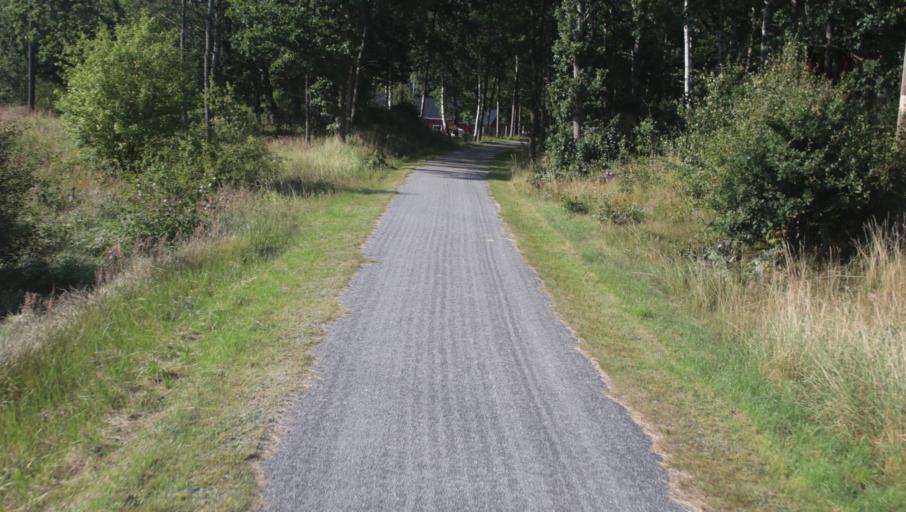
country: SE
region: Blekinge
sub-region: Karlshamns Kommun
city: Svangsta
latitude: 56.3880
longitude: 14.6754
